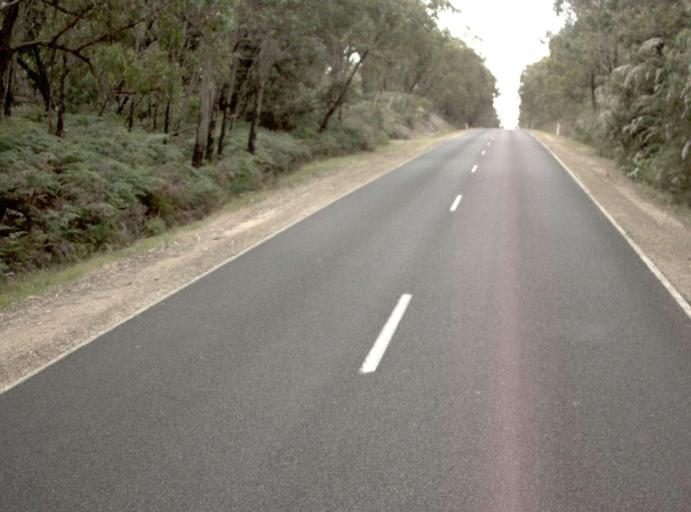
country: AU
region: Victoria
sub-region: Latrobe
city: Traralgon
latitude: -38.3985
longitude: 146.8177
